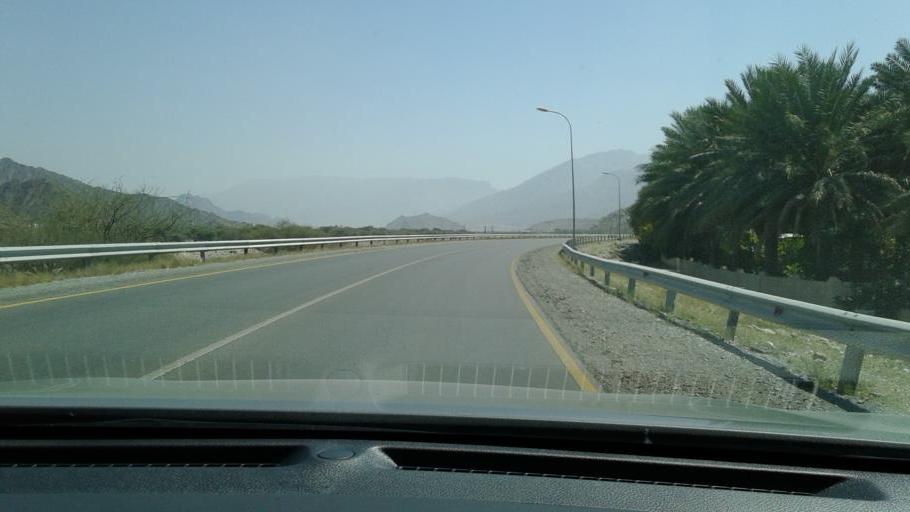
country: OM
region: Al Batinah
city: Rustaq
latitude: 23.3910
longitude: 57.4431
